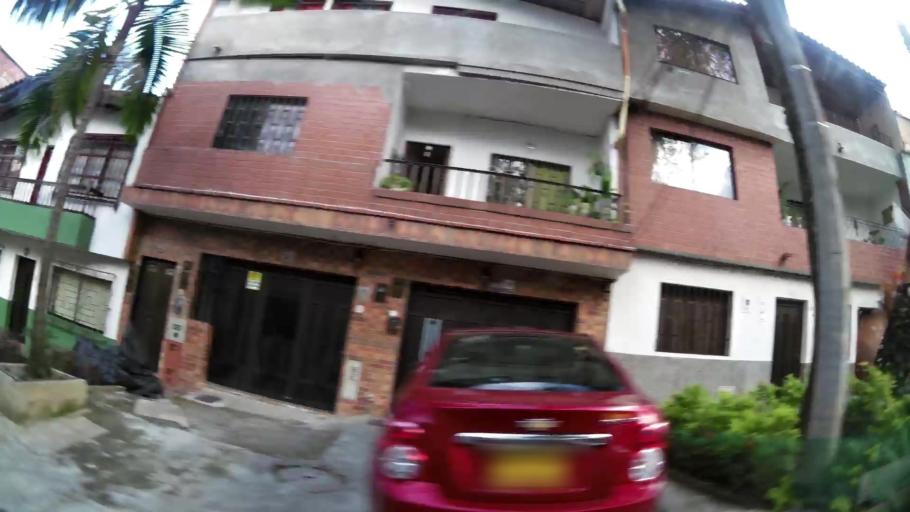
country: CO
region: Antioquia
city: Envigado
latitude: 6.1703
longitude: -75.5815
